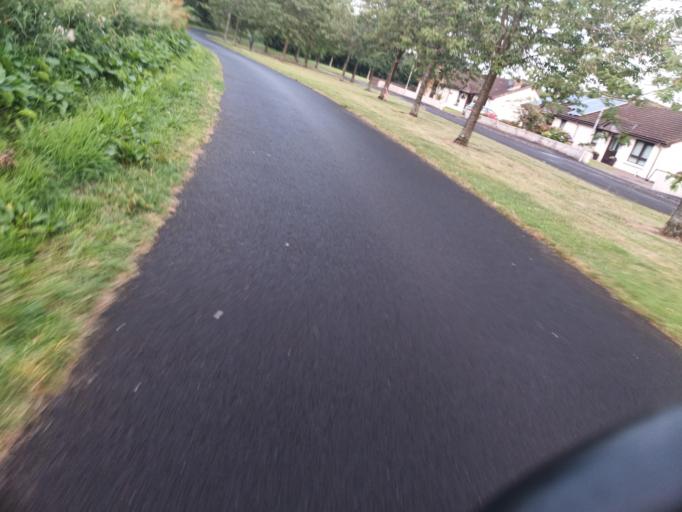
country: GB
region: Northern Ireland
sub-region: Castlereagh District
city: Dundonald
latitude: 54.5850
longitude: -5.7932
